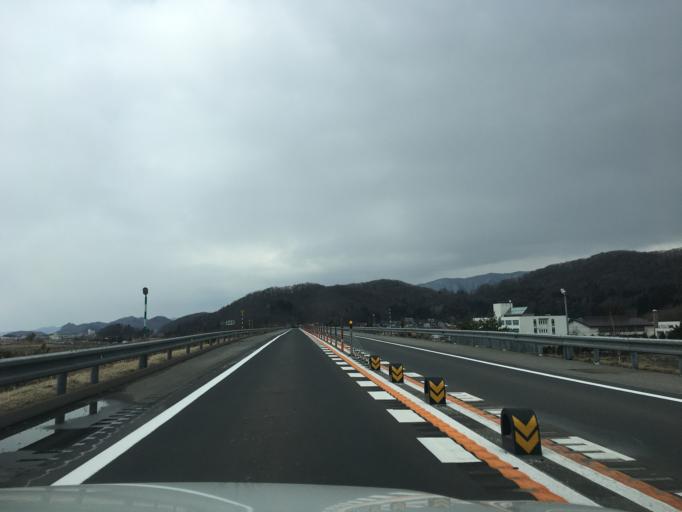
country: JP
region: Aomori
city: Aomori Shi
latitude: 40.8097
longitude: 140.8015
